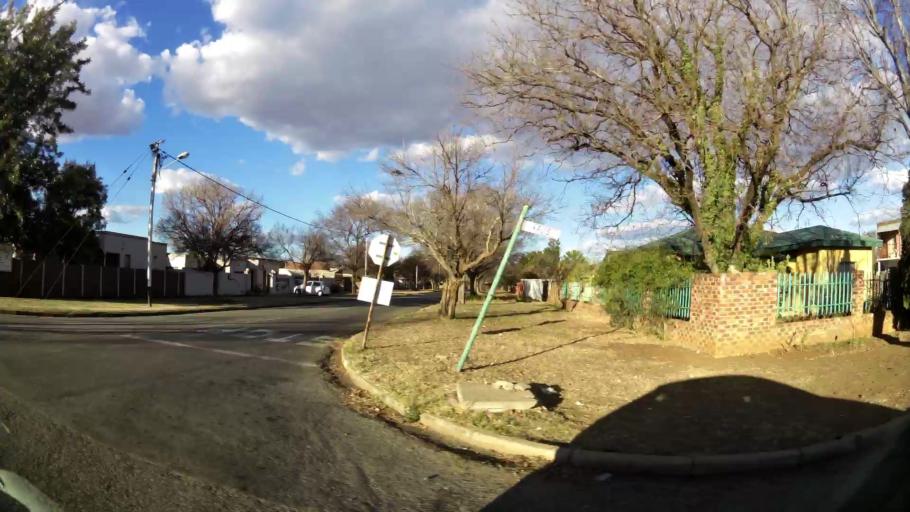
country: ZA
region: North-West
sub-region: Dr Kenneth Kaunda District Municipality
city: Potchefstroom
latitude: -26.7379
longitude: 27.0836
